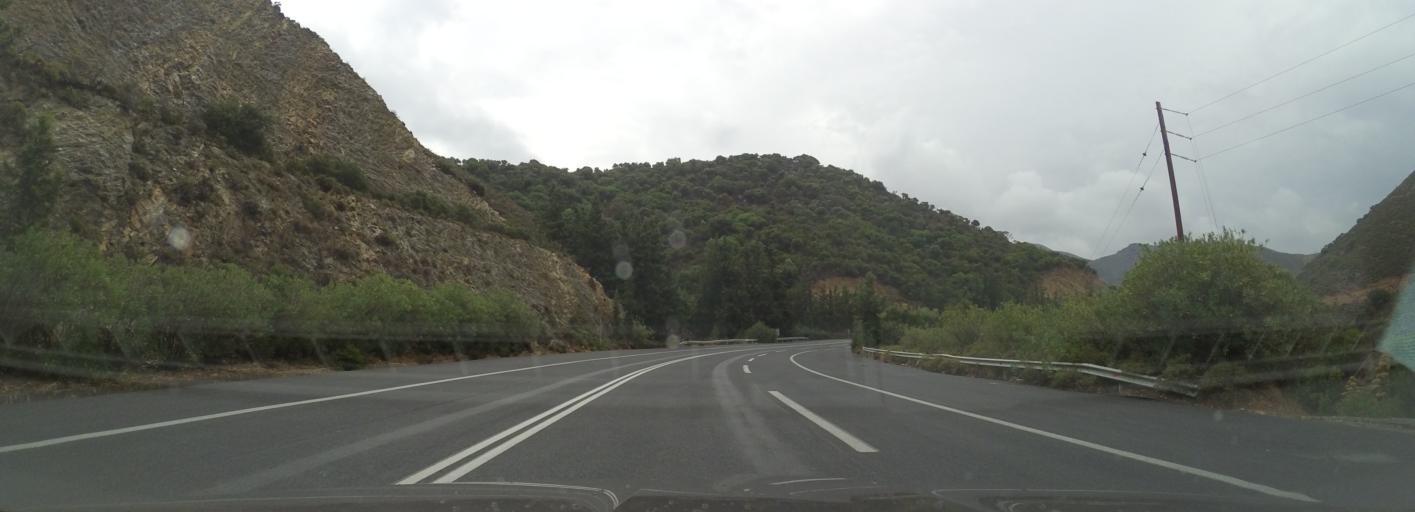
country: GR
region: Crete
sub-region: Nomos Rethymnis
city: Anogeia
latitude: 35.3909
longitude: 24.9460
